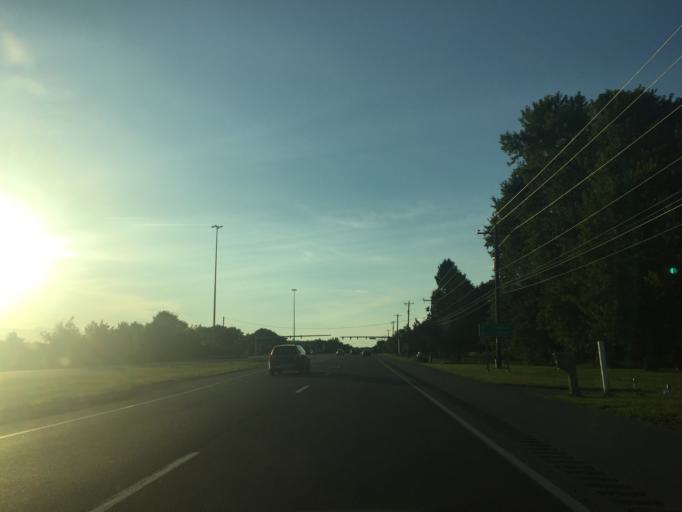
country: US
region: Delaware
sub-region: Kent County
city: Smyrna
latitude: 39.3338
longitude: -75.6277
